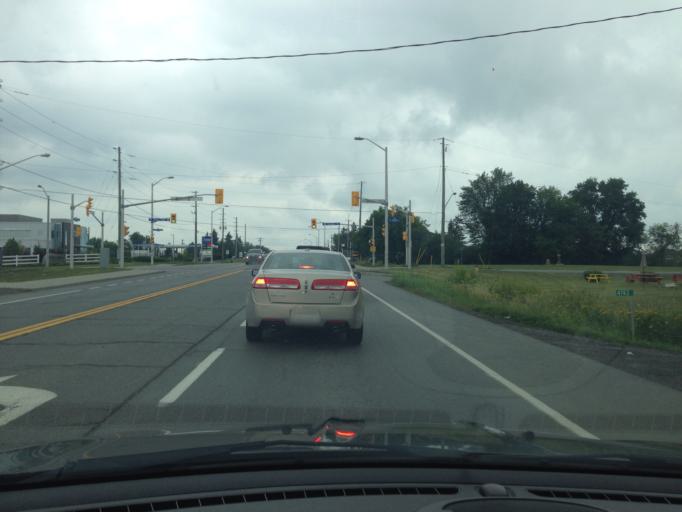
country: CA
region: Ontario
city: Ottawa
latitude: 45.3231
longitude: -75.5952
